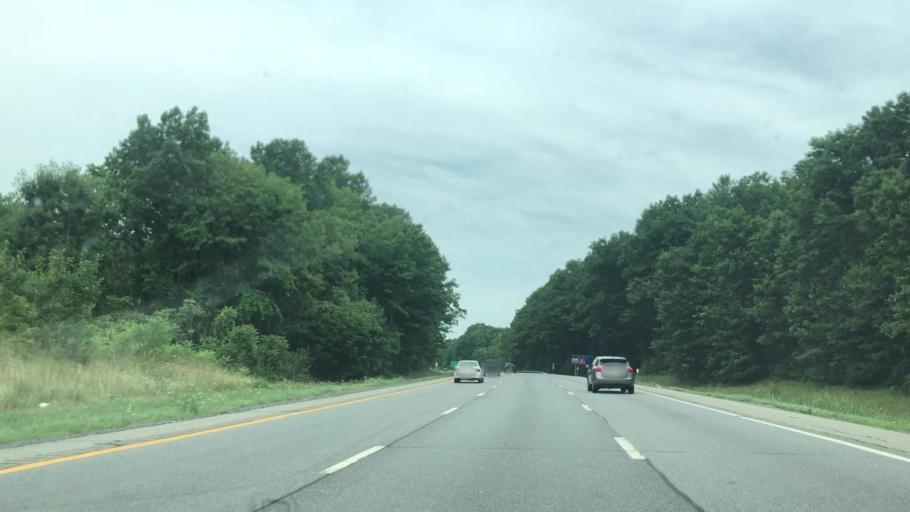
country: US
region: New York
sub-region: Saratoga County
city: Country Knolls
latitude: 42.8949
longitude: -73.7804
